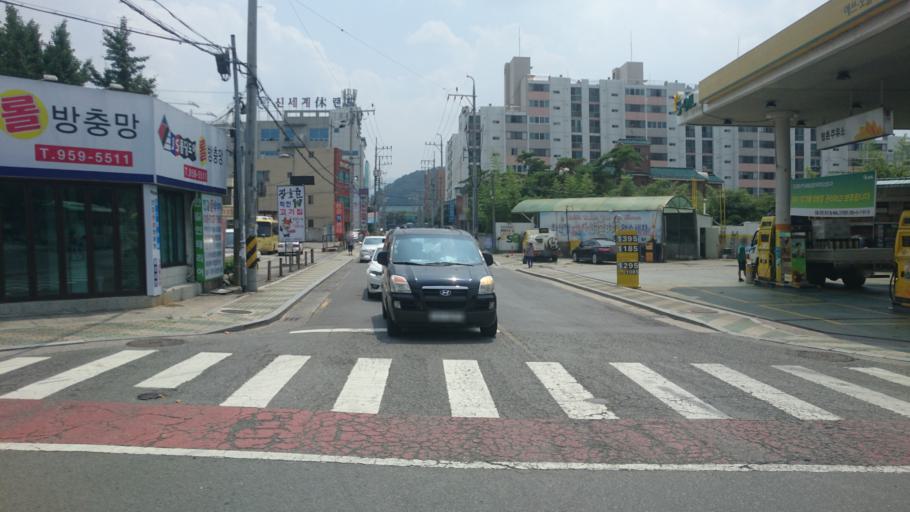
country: KR
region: Gyeongsangbuk-do
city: Gyeongsan-si
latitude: 35.8782
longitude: 128.6747
